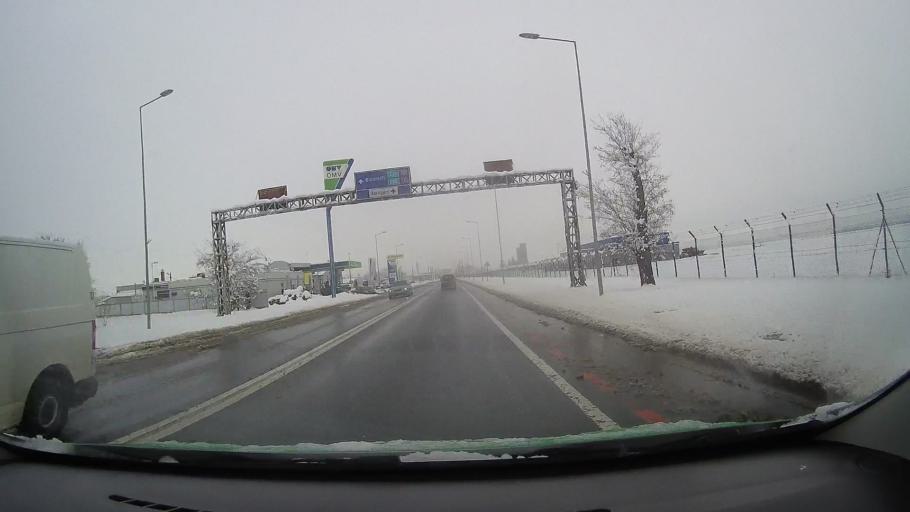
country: RO
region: Sibiu
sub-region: Comuna Sura Mica
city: Sura Mica
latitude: 45.7891
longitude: 24.0847
